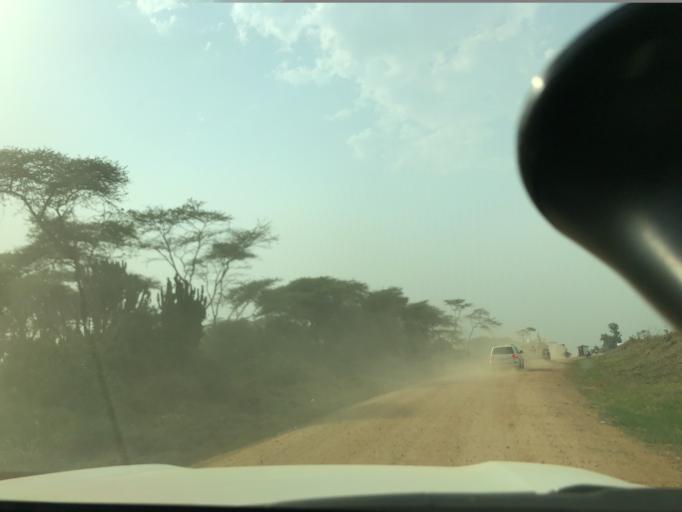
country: UG
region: Western Region
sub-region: Kasese District
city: Kilembe
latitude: 0.0577
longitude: 29.6664
